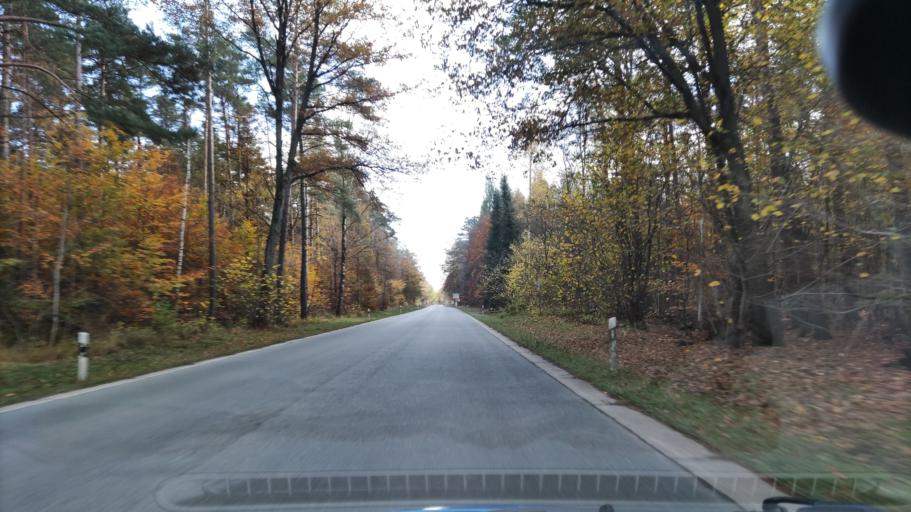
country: DE
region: Lower Saxony
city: Munster
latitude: 53.0047
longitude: 10.1150
